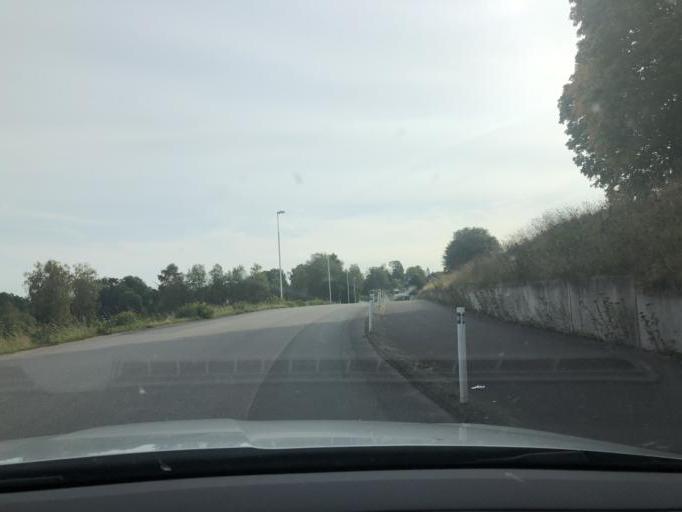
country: SE
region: Joenkoeping
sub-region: Vetlanda Kommun
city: Ekenassjon
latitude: 57.5158
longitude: 14.9070
